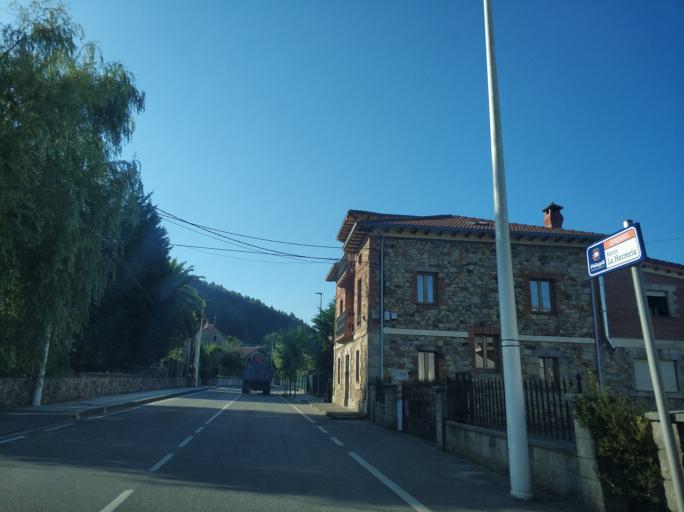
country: ES
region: Cantabria
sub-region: Provincia de Cantabria
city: Polanco
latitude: 43.3681
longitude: -3.9587
